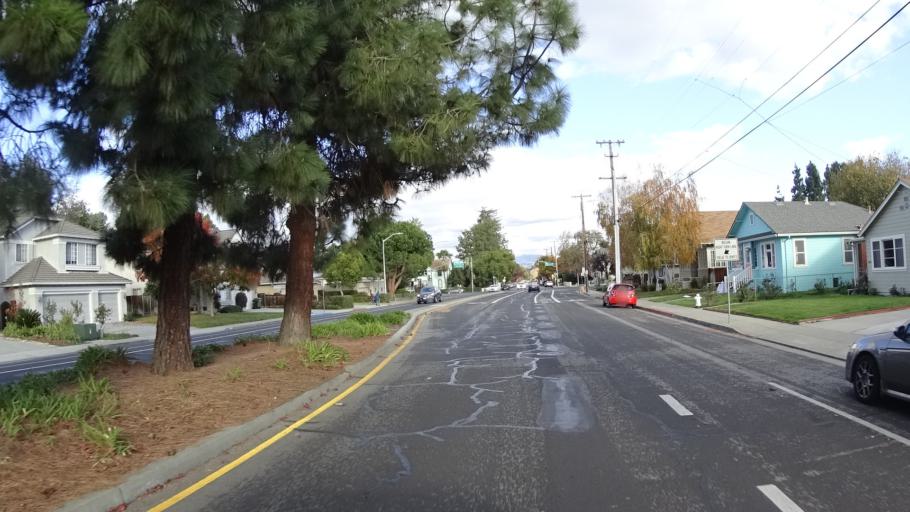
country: US
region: California
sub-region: Santa Clara County
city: Santa Clara
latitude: 37.3458
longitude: -121.9525
